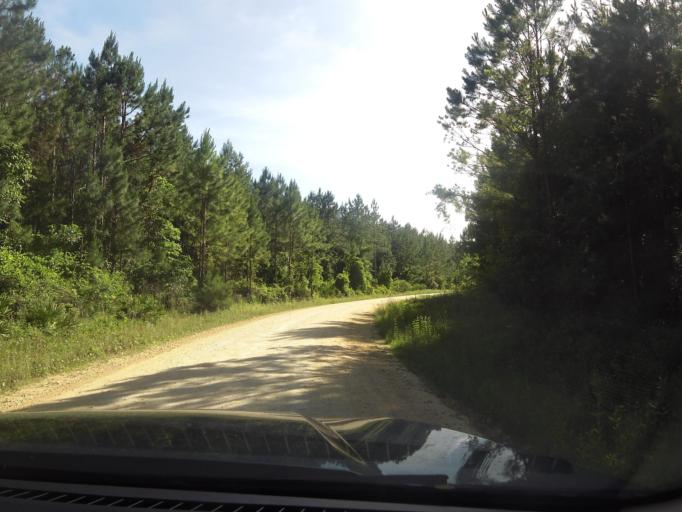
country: US
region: Florida
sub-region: Nassau County
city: Callahan
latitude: 30.5734
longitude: -81.7751
